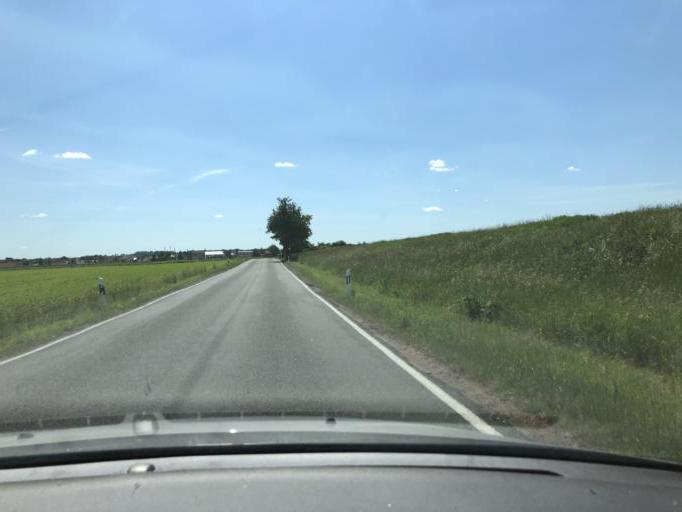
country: DE
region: Saxony
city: Nerchau
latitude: 51.2821
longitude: 12.7790
